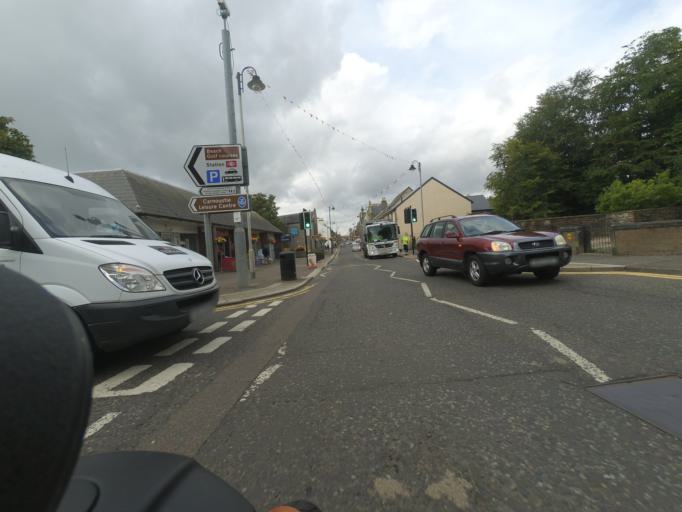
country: GB
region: Scotland
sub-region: Angus
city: Carnoustie
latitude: 56.5017
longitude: -2.7072
